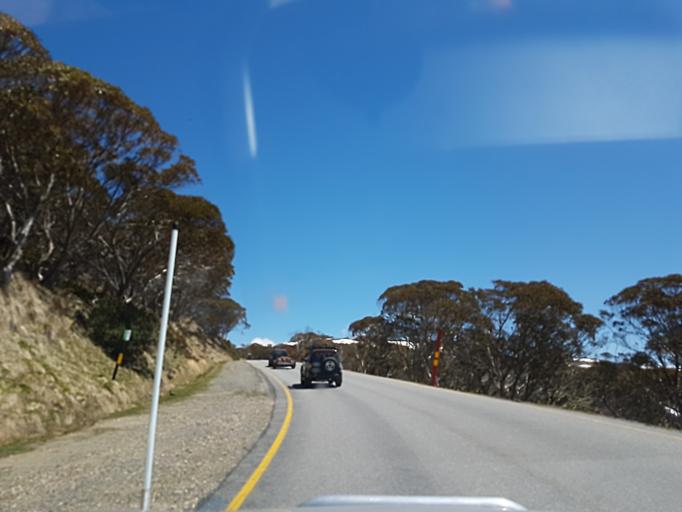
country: AU
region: Victoria
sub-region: Alpine
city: Mount Beauty
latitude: -36.9927
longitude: 147.1592
